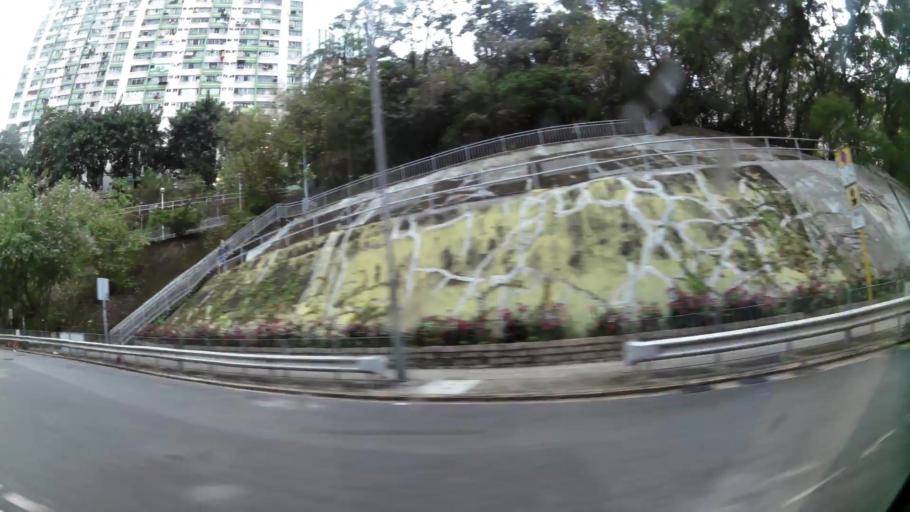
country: HK
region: Tsuen Wan
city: Tsuen Wan
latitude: 22.3677
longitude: 114.1239
